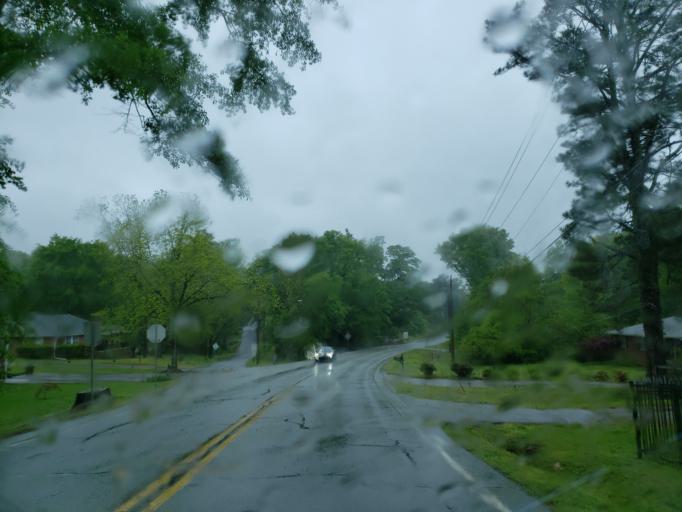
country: US
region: Georgia
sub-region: Carroll County
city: Villa Rica
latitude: 33.7377
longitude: -84.9224
